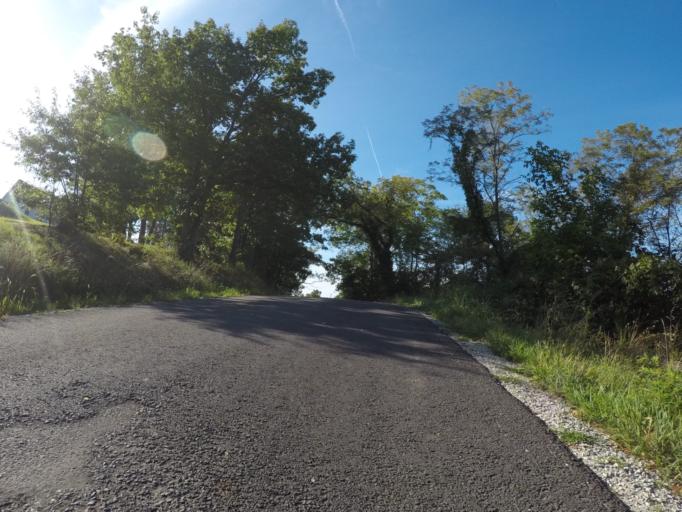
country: US
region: Ohio
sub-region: Lawrence County
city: Burlington
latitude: 38.5242
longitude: -82.5244
